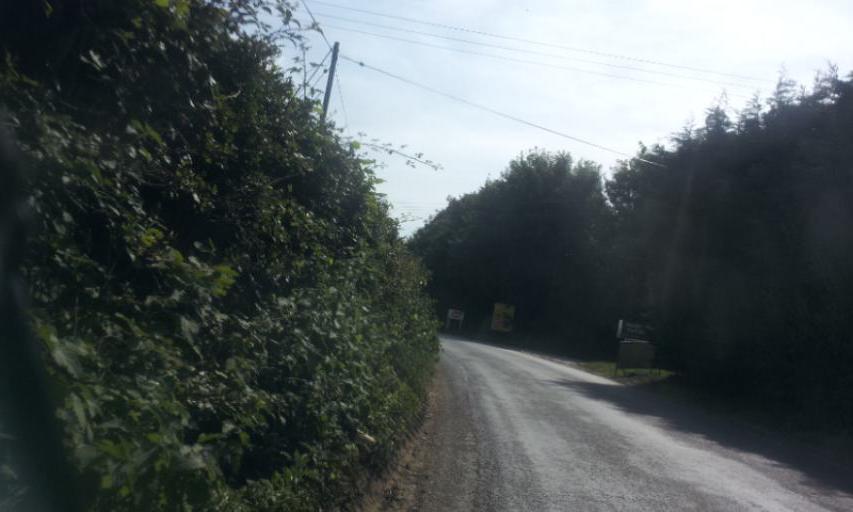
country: GB
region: England
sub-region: Kent
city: Newington
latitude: 51.3262
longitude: 0.6935
